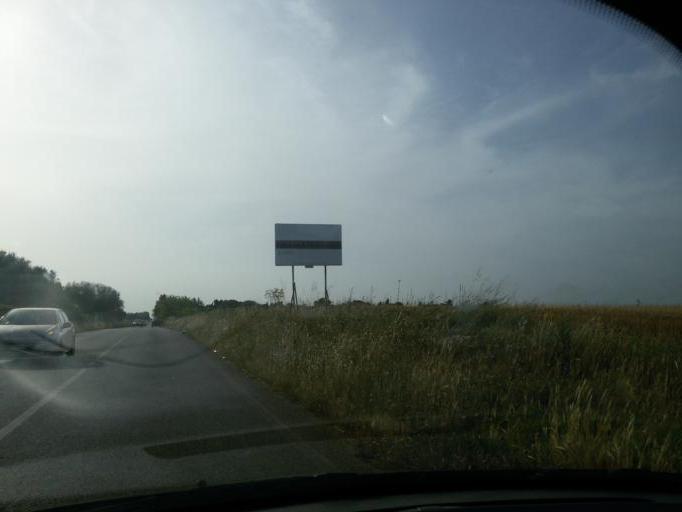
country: IT
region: Apulia
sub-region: Provincia di Lecce
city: Porto Cesareo
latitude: 40.2759
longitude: 17.8969
